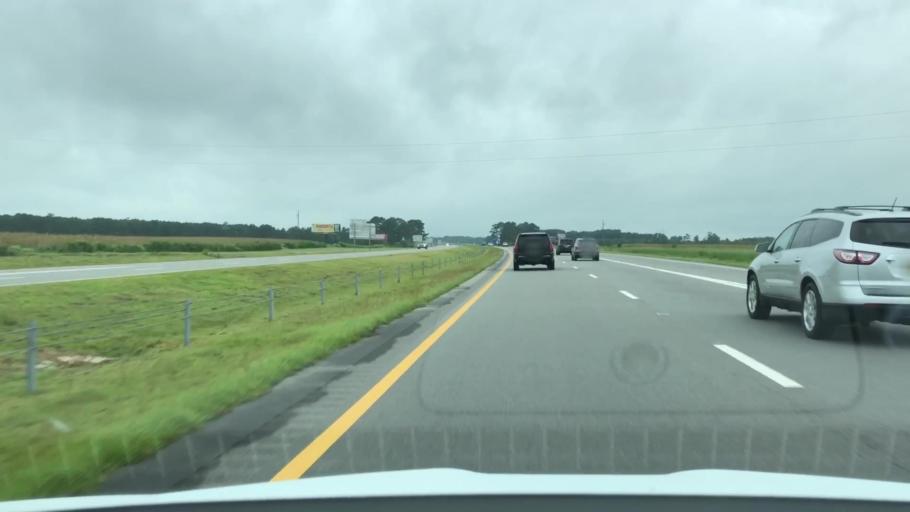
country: US
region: North Carolina
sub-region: Wayne County
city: Elroy
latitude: 35.4140
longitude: -77.9016
